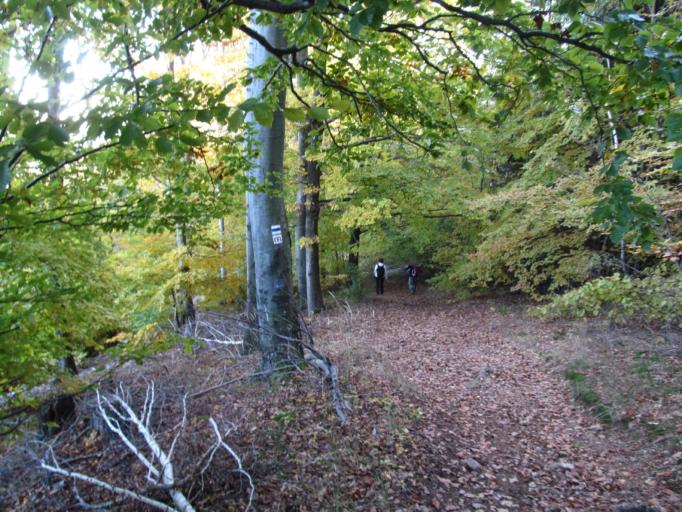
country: HU
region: Heves
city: Paradsasvar
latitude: 47.9103
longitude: 19.9469
